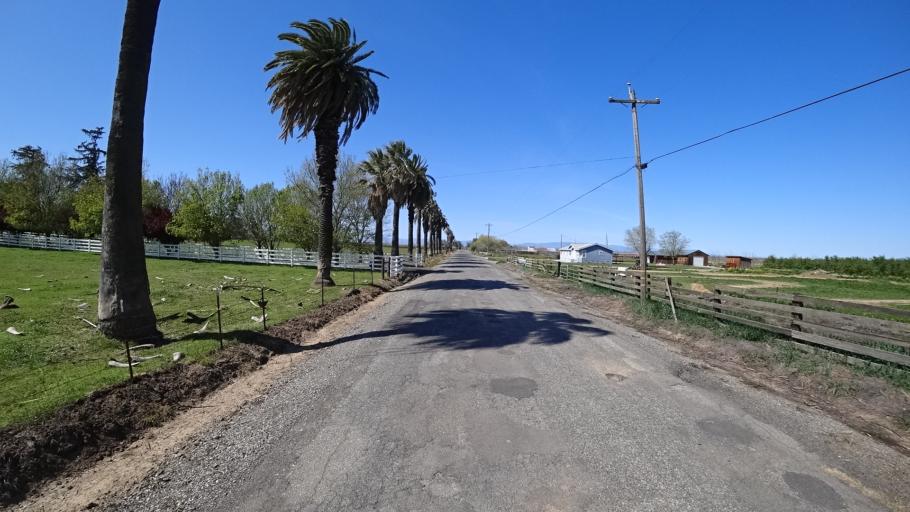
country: US
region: California
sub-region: Glenn County
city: Orland
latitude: 39.7969
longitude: -122.1099
